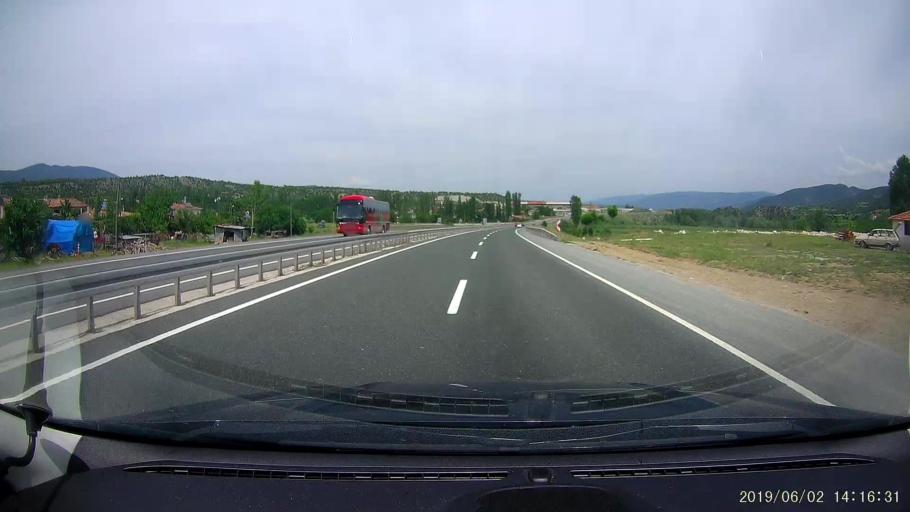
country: TR
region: Kastamonu
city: Tosya
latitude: 40.9493
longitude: 33.9095
